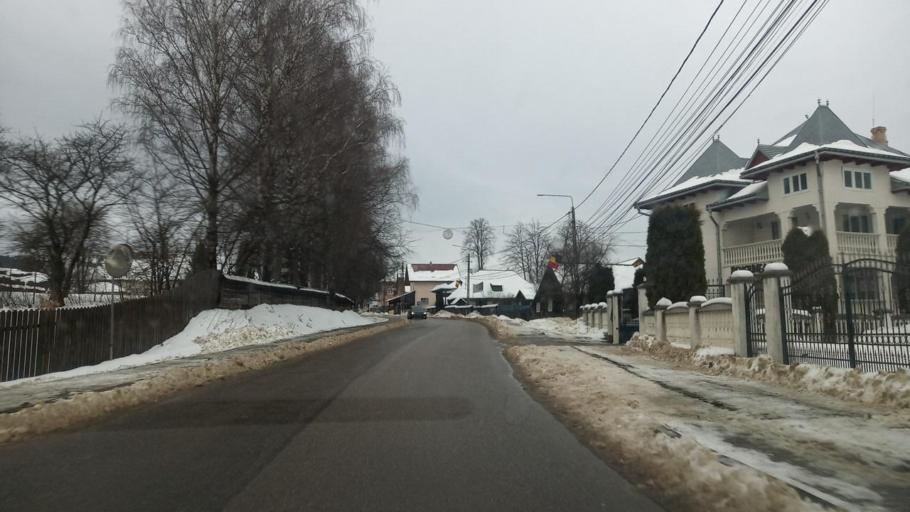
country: RO
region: Suceava
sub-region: Comuna Manastirea Humorului
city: Manastirea Humorului
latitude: 47.5931
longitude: 25.8596
